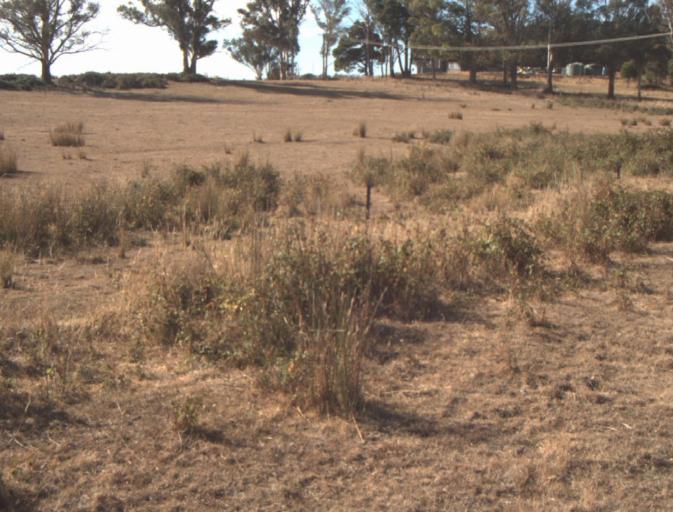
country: AU
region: Tasmania
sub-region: Dorset
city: Bridport
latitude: -41.1431
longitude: 147.2124
